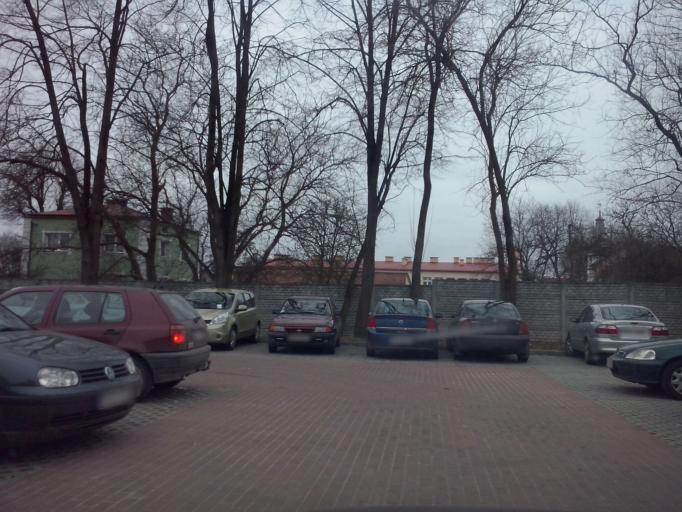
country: PL
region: Subcarpathian Voivodeship
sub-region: Powiat nizanski
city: Nisko
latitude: 50.5172
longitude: 22.1440
